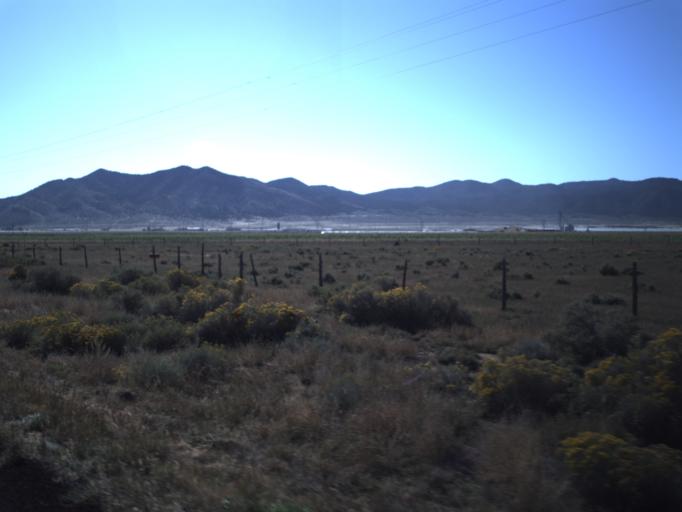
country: US
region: Utah
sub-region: Washington County
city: Enterprise
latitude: 37.6827
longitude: -113.5819
